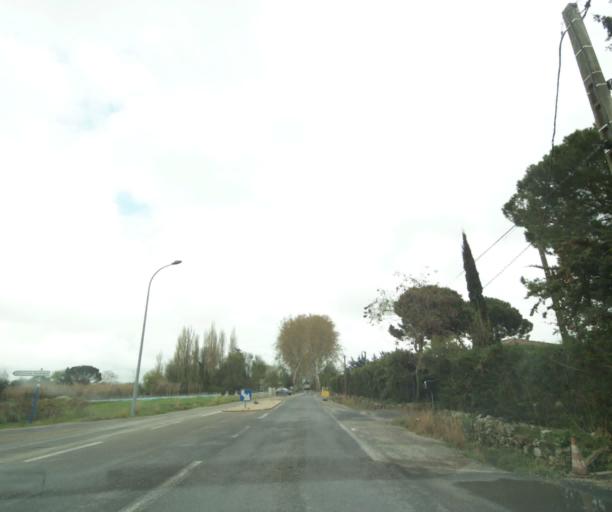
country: FR
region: Languedoc-Roussillon
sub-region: Departement de l'Herault
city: Cournonterral
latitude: 43.5521
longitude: 3.7276
